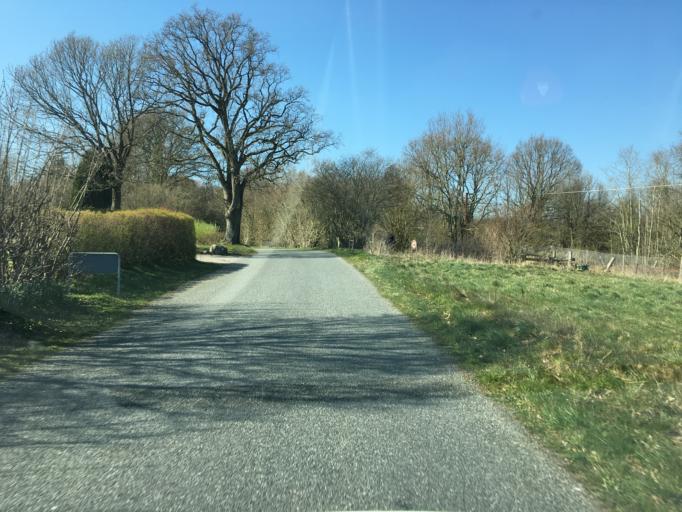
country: DK
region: South Denmark
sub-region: Aabenraa Kommune
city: Krusa
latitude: 54.9261
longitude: 9.4413
